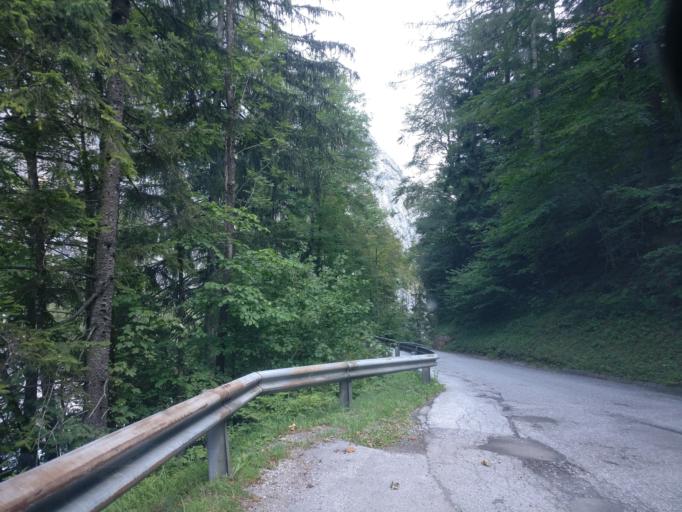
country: AT
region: Styria
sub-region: Politischer Bezirk Liezen
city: Johnsbach
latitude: 47.5819
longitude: 14.5506
